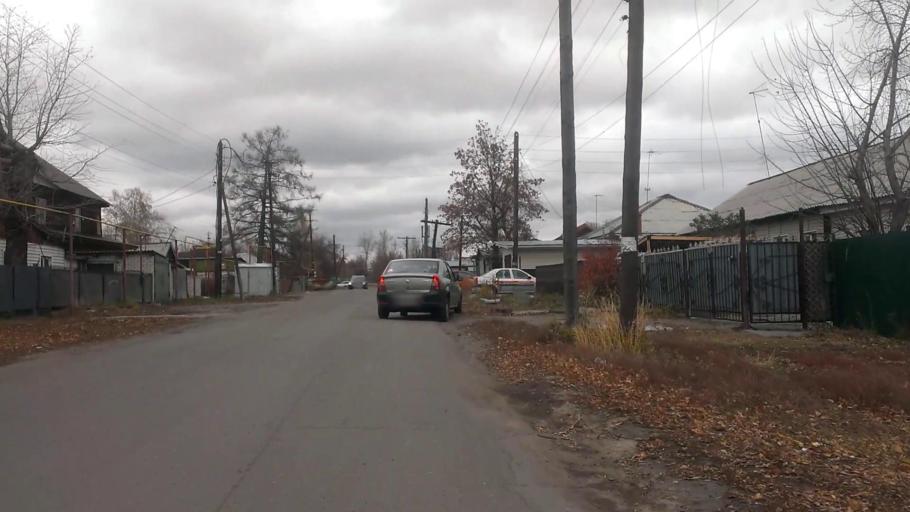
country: RU
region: Altai Krai
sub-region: Gorod Barnaulskiy
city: Barnaul
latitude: 53.3520
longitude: 83.7527
